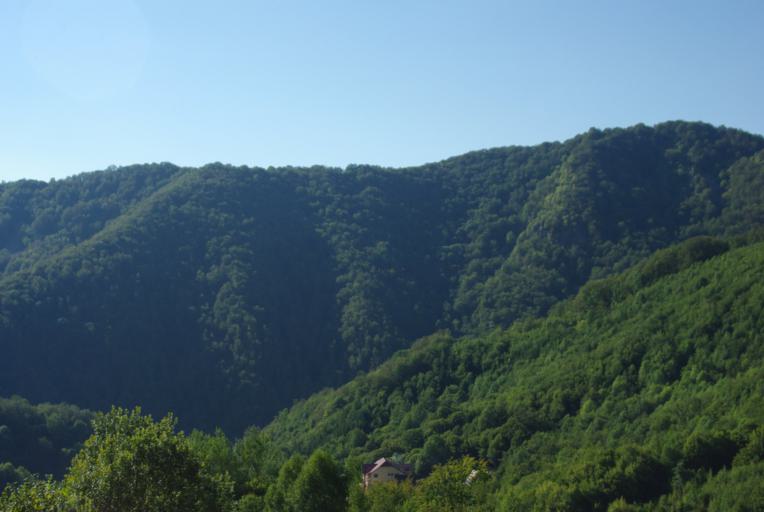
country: RO
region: Bihor
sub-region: Comuna Pietroasa
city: Pietroasa
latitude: 46.5997
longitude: 22.6554
